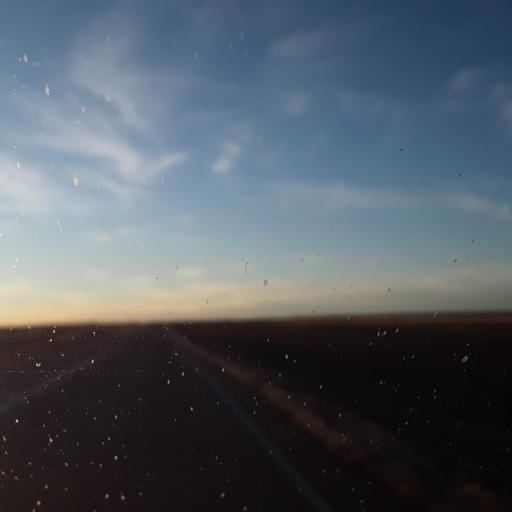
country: US
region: Colorado
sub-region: Cheyenne County
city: Cheyenne Wells
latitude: 38.8097
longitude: -102.4092
